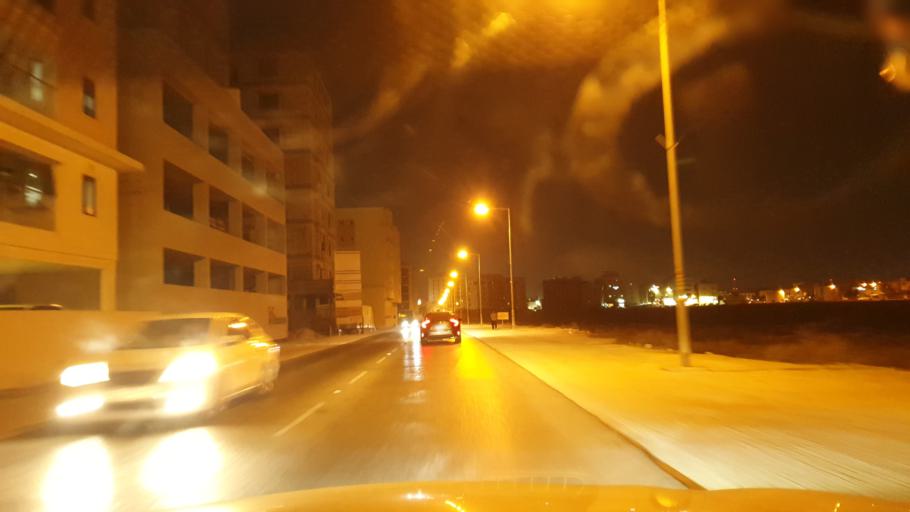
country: BH
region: Northern
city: Madinat `Isa
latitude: 26.1855
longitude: 50.4820
